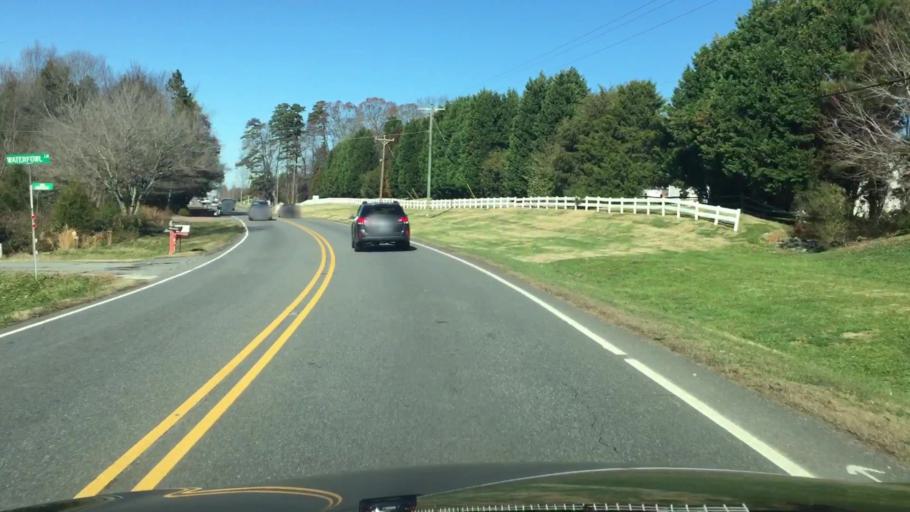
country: US
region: North Carolina
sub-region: Iredell County
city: Mooresville
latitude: 35.5687
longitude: -80.8661
